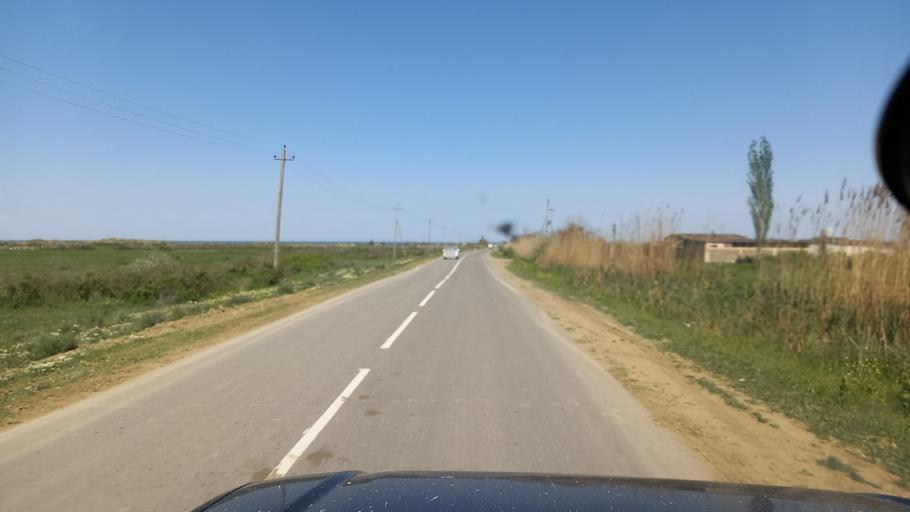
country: RU
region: Dagestan
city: Khazar
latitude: 41.9464
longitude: 48.3493
